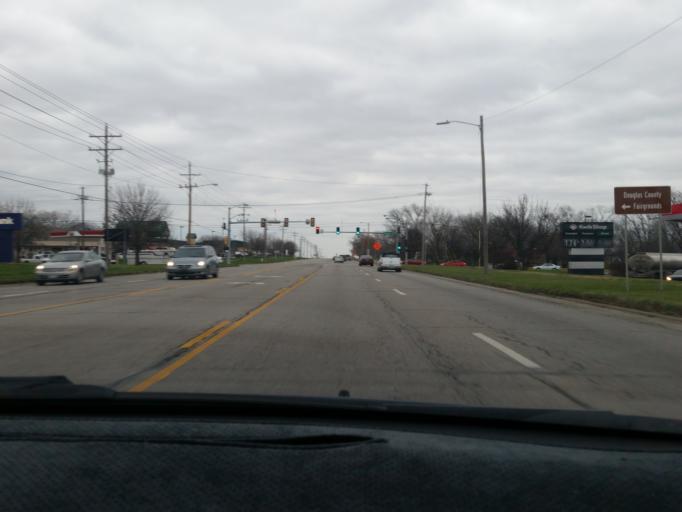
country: US
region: Kansas
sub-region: Douglas County
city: Lawrence
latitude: 38.9427
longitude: -95.2156
